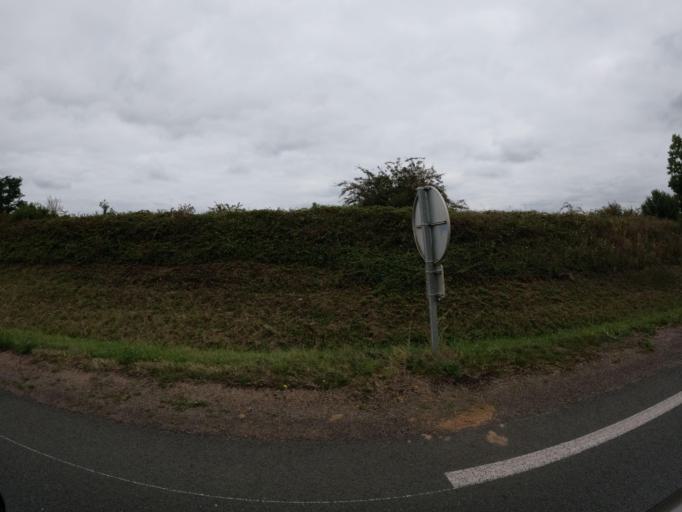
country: FR
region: Pays de la Loire
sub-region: Departement de la Vendee
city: Fontenay-le-Comte
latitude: 46.4661
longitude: -0.8461
